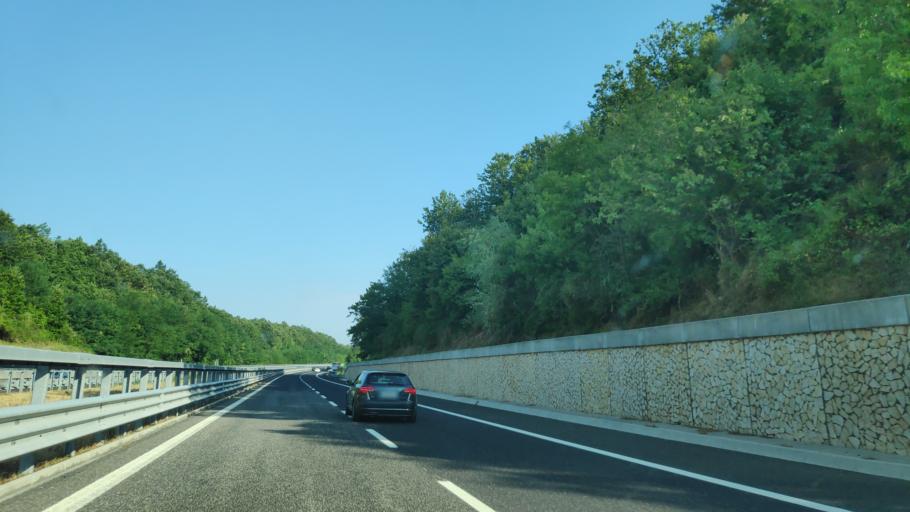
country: IT
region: Campania
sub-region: Provincia di Salerno
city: Casalbuono
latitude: 40.2357
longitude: 15.6627
